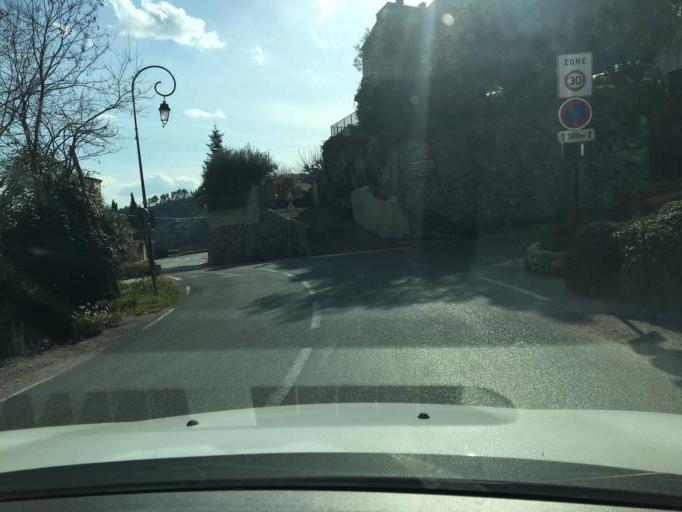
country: FR
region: Provence-Alpes-Cote d'Azur
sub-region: Departement du Var
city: Callas
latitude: 43.5933
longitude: 6.5399
